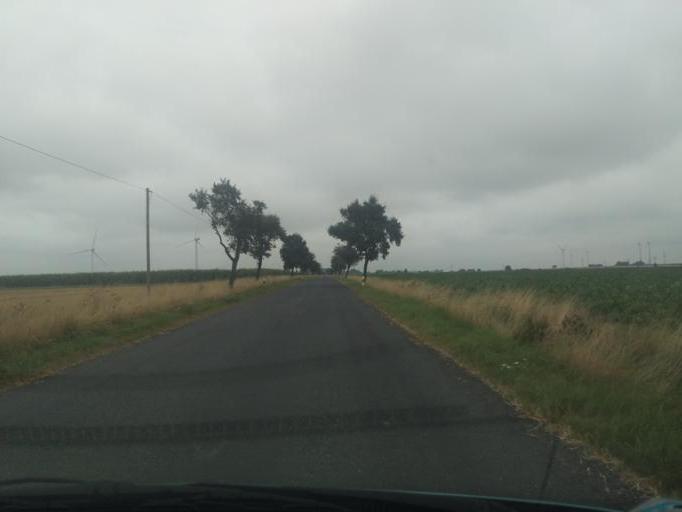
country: DE
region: Lower Saxony
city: Hohenhameln
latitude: 52.2502
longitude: 10.1142
